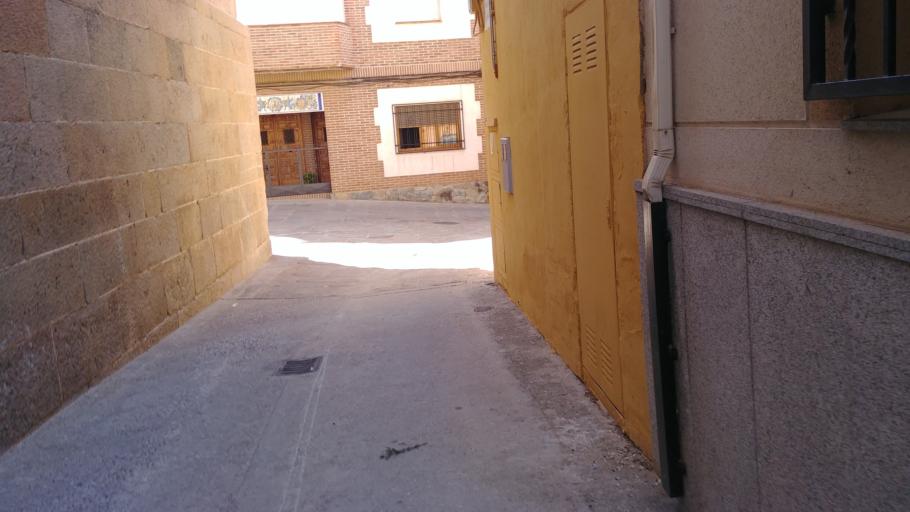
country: ES
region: Castille-La Mancha
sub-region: Province of Toledo
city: Oropesa
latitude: 39.9193
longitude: -5.1727
